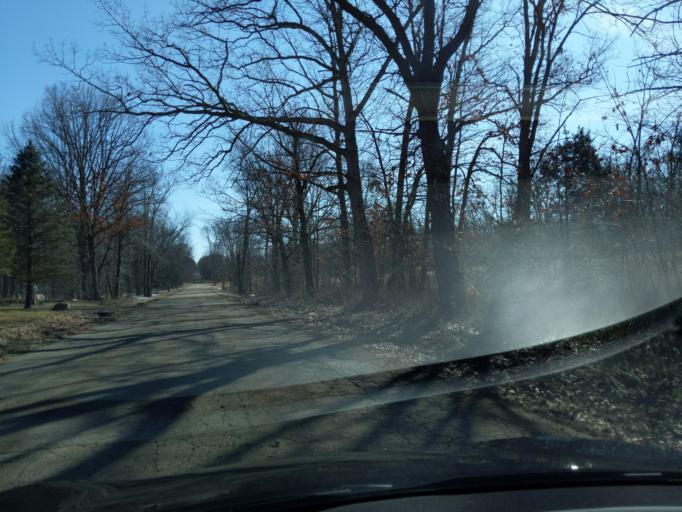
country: US
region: Michigan
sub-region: Ingham County
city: Leslie
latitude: 42.4054
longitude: -84.4285
